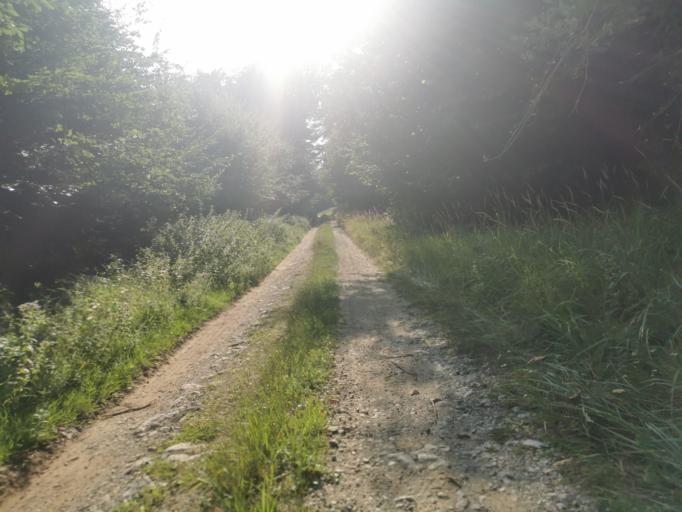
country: SK
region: Trenciansky
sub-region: Okres Myjava
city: Myjava
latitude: 48.8262
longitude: 17.6141
